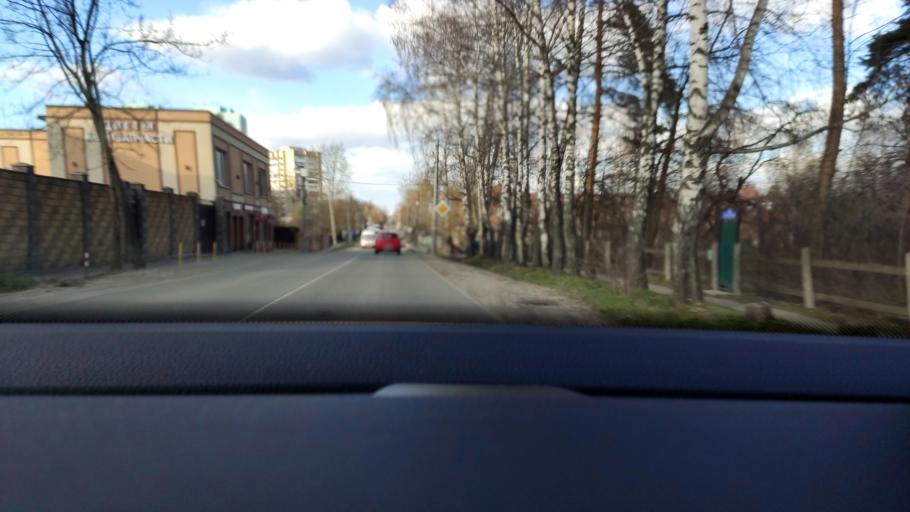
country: RU
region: Moskovskaya
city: Saltykovka
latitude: 55.7739
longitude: 37.8989
